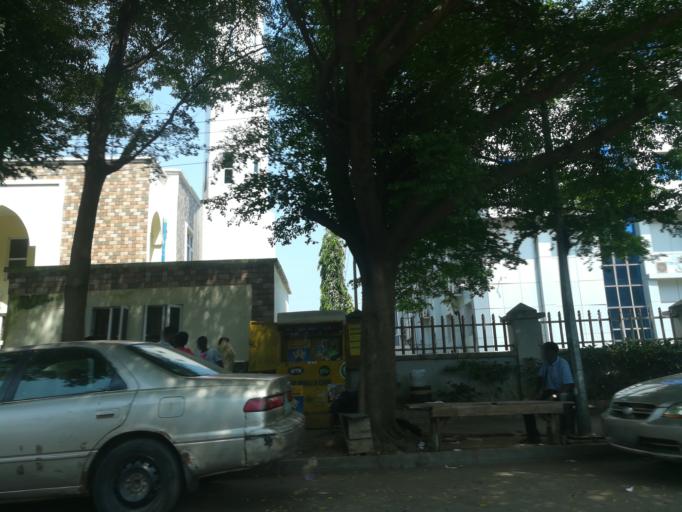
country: NG
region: Abuja Federal Capital Territory
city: Abuja
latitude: 9.0670
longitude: 7.4437
